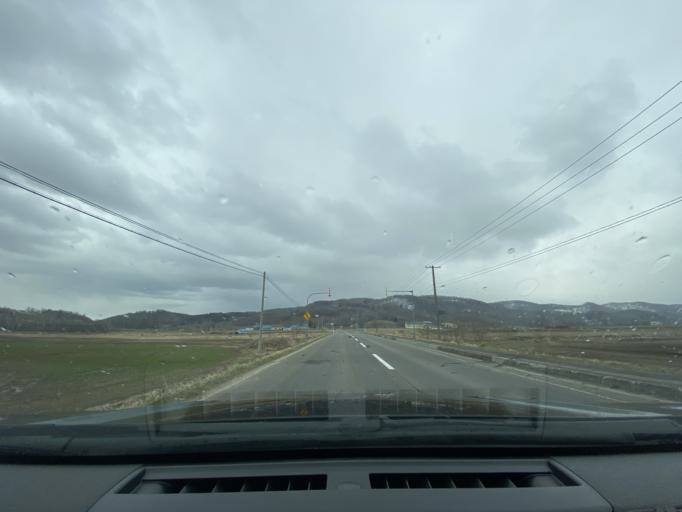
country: JP
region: Hokkaido
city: Nayoro
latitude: 44.1699
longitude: 142.2596
